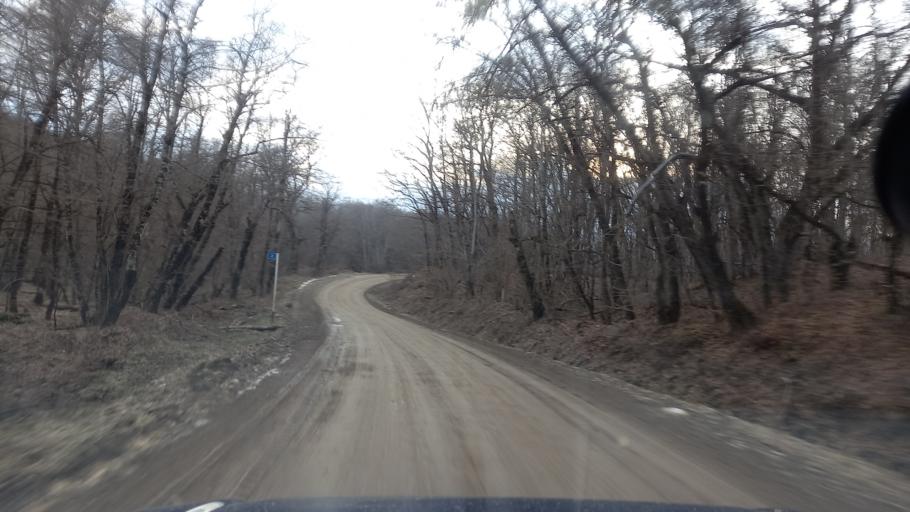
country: RU
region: Adygeya
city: Kamennomostskiy
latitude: 44.1394
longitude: 40.2655
